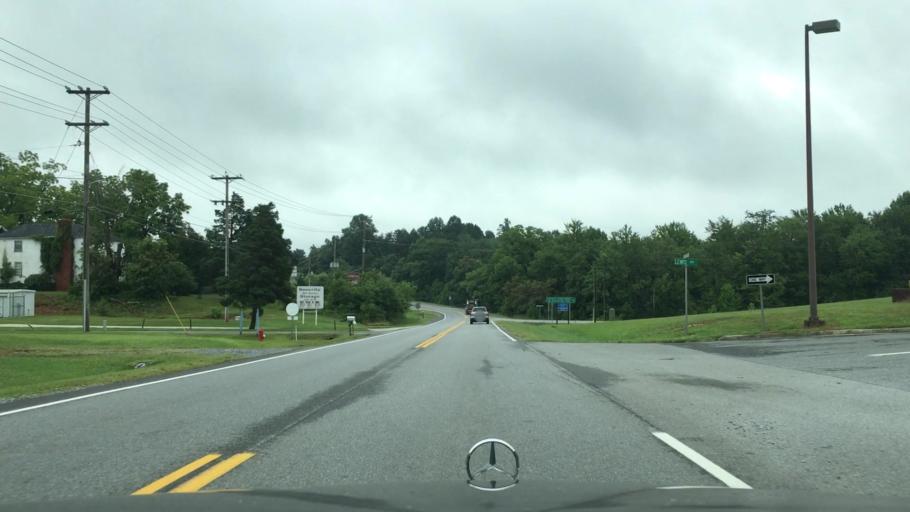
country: US
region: Virginia
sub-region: Campbell County
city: Timberlake
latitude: 37.3284
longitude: -79.2192
